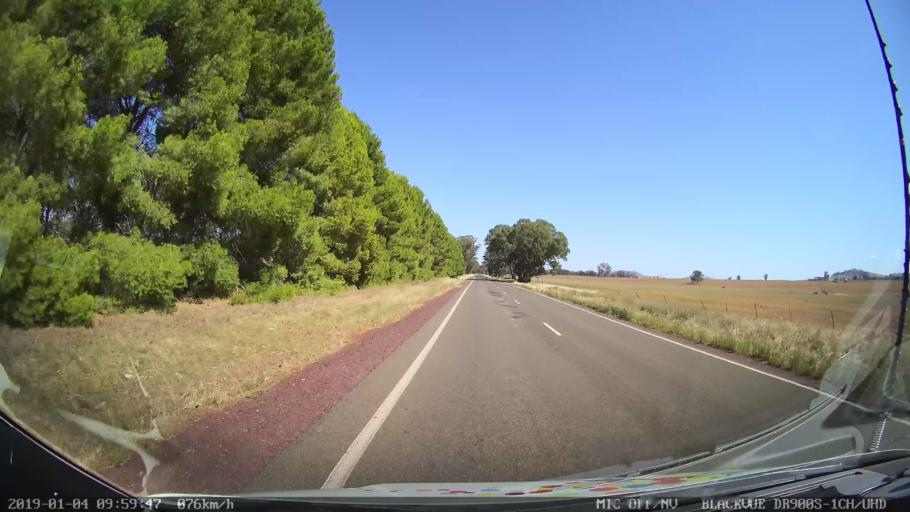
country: AU
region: New South Wales
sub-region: Cabonne
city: Canowindra
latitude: -33.5042
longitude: 148.3837
